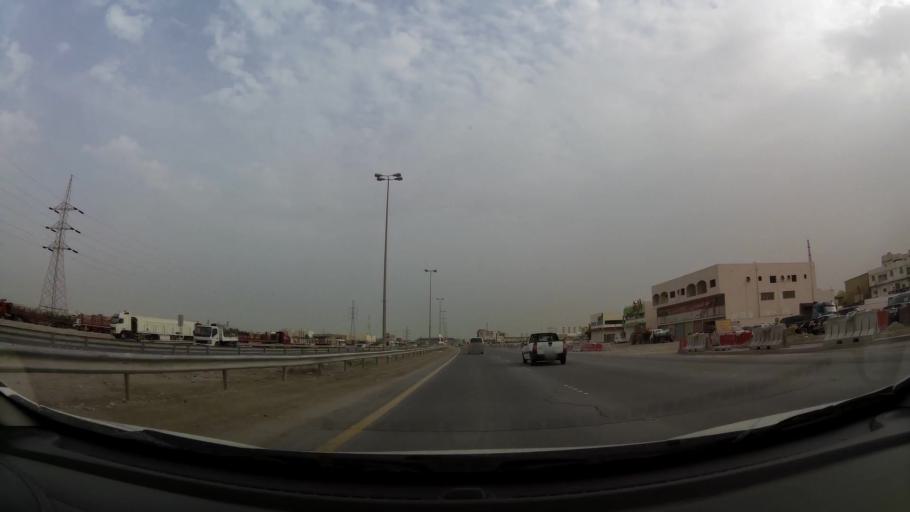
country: BH
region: Northern
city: Ar Rifa'
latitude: 26.1324
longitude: 50.5857
